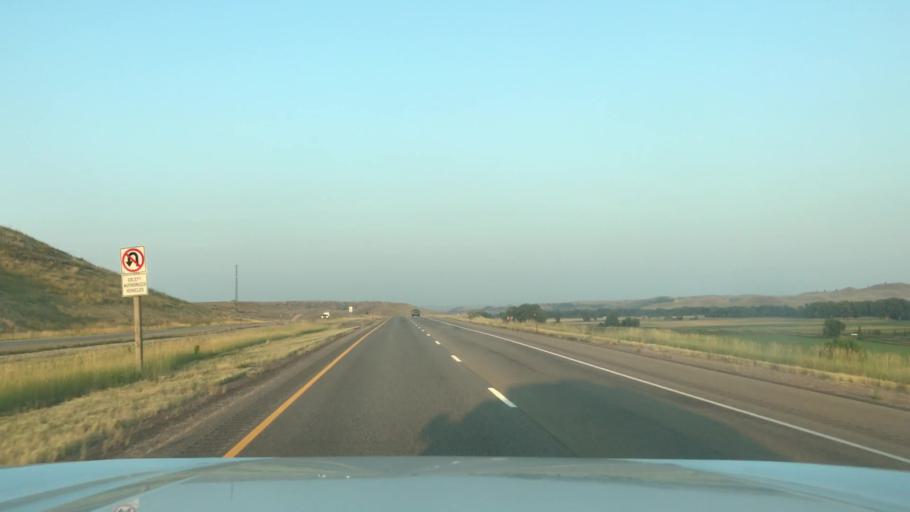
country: US
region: Wyoming
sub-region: Sheridan County
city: Sheridan
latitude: 44.9145
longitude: -107.0782
